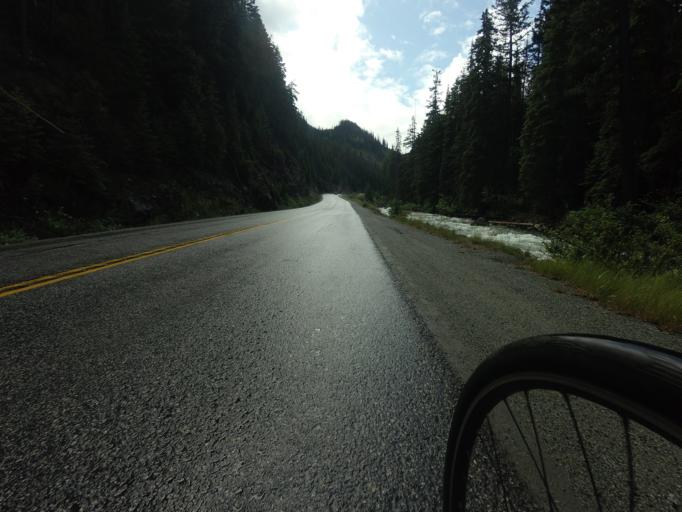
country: CA
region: British Columbia
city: Lillooet
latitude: 50.4392
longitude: -122.2536
